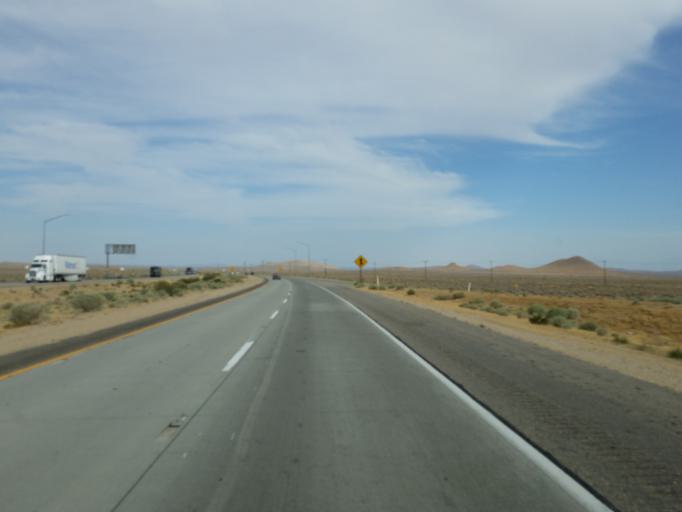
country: US
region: California
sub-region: Kern County
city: Mojave
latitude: 35.0351
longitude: -118.1041
